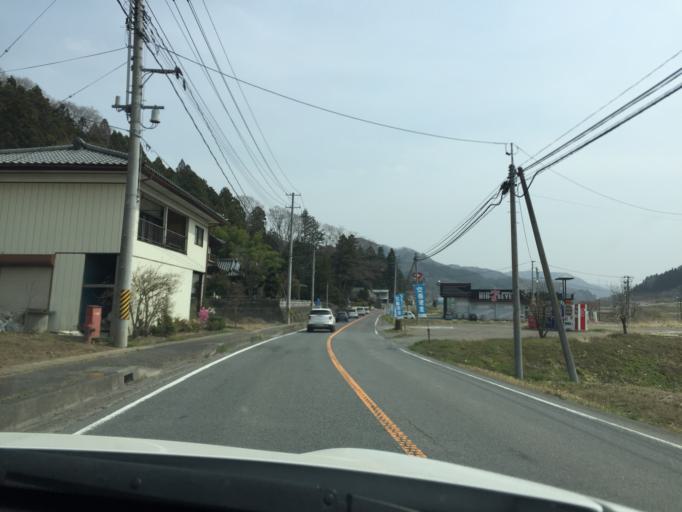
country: JP
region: Fukushima
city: Ishikawa
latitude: 37.1441
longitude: 140.4864
